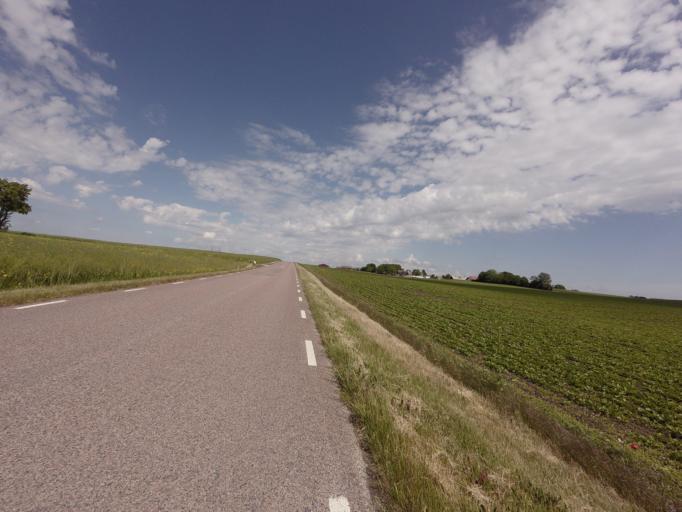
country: SE
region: Skane
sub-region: Trelleborgs Kommun
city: Skare
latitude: 55.4209
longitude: 13.1041
